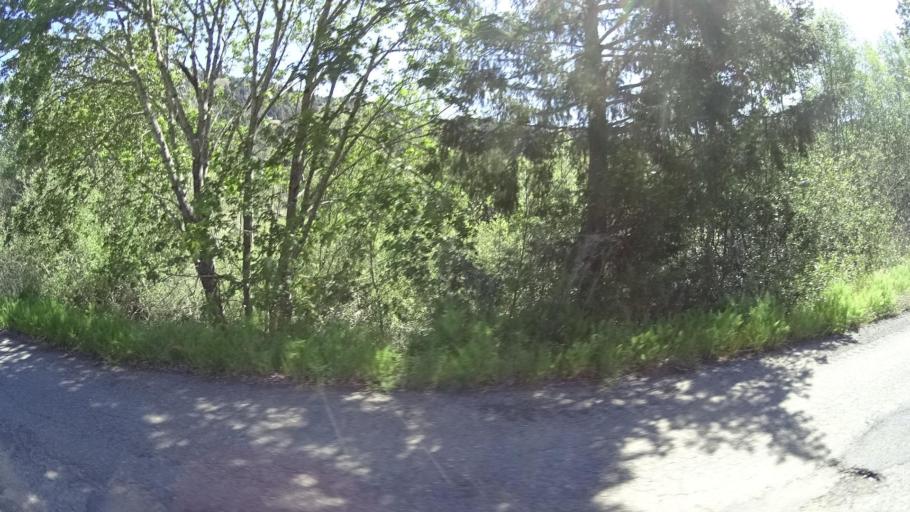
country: US
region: California
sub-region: Humboldt County
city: Rio Dell
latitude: 40.2400
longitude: -124.1220
